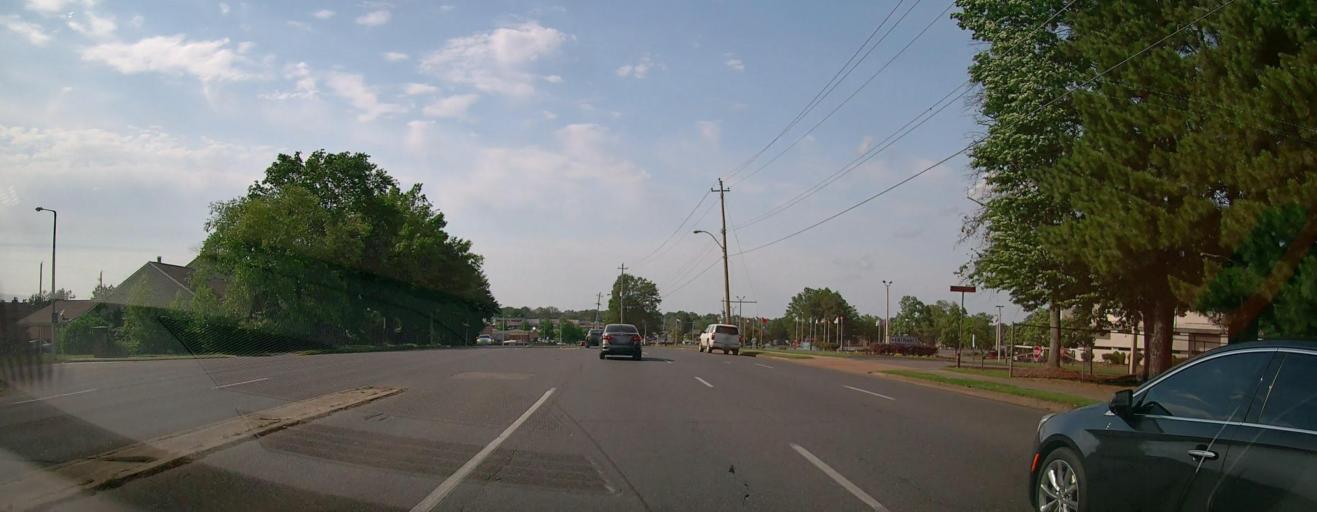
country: US
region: Tennessee
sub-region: Shelby County
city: Germantown
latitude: 35.0461
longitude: -89.8431
